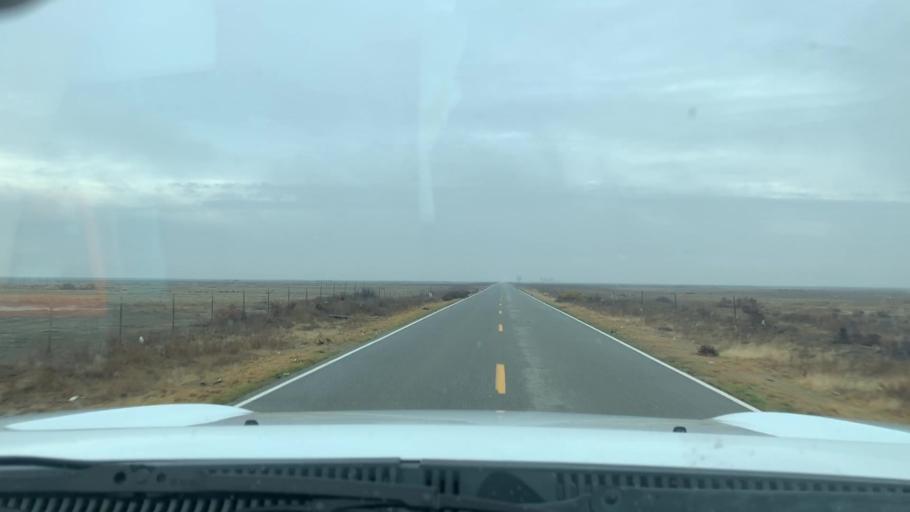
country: US
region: California
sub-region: Kern County
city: Lost Hills
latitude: 35.6457
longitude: -119.5801
